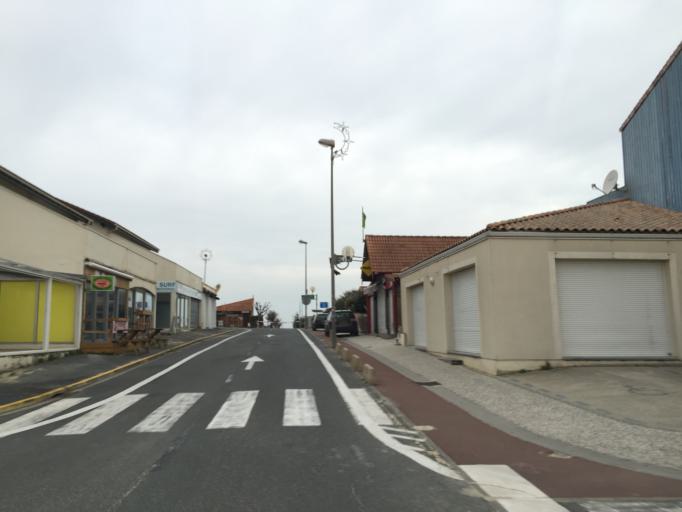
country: FR
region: Aquitaine
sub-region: Departement de la Gironde
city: Hourtin
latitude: 45.2231
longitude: -1.1688
